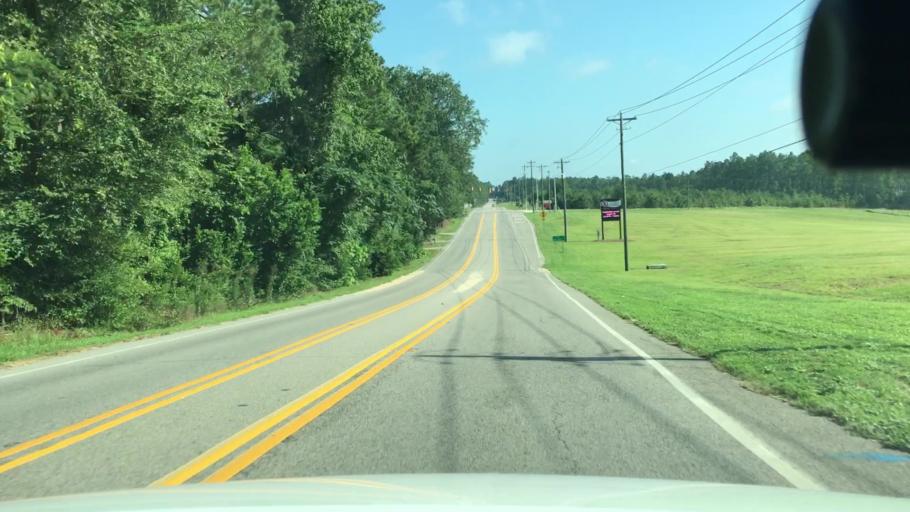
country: US
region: South Carolina
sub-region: Aiken County
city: Graniteville
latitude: 33.5816
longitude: -81.8360
